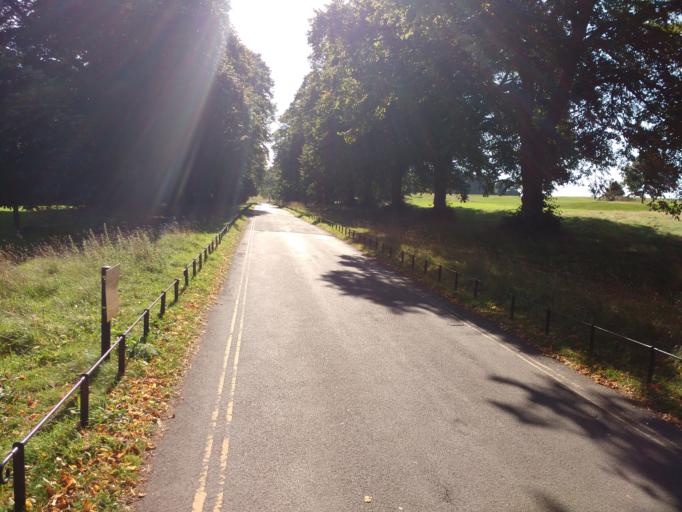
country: GB
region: England
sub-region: North Somerset
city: Long Ashton
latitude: 51.4511
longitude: -2.6380
